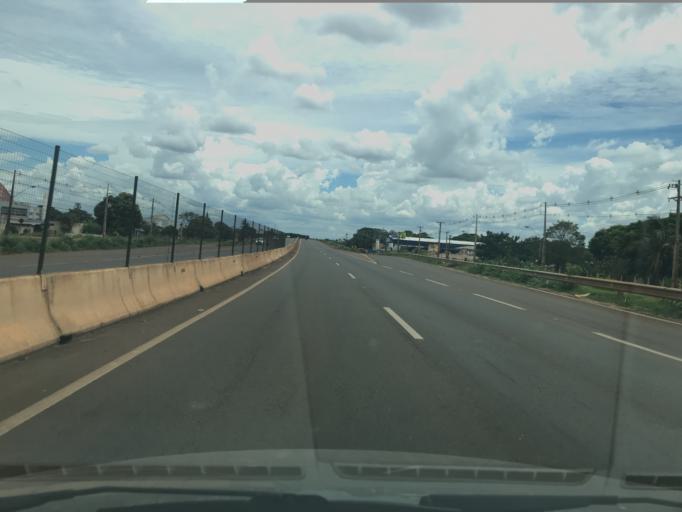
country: BR
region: Parana
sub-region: Paicandu
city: Paicandu
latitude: -23.4479
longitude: -52.0017
